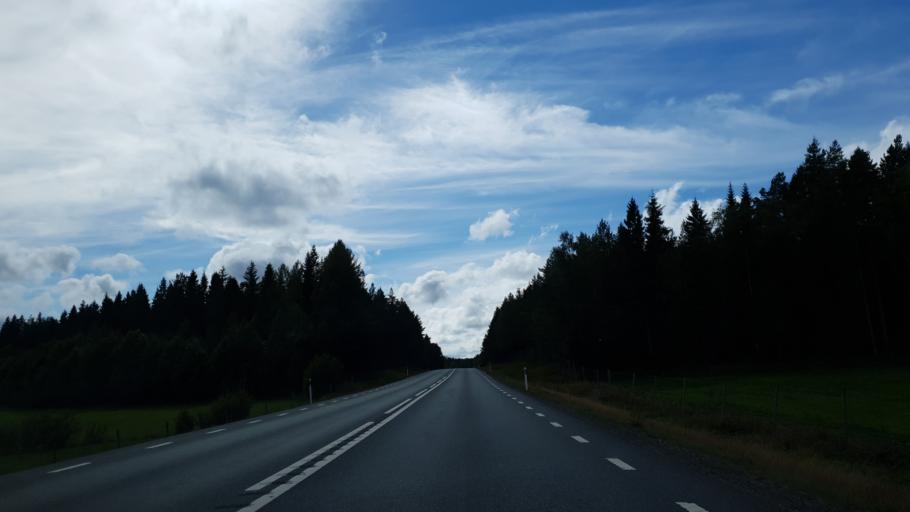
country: SE
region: Vaesterbotten
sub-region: Robertsfors Kommun
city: Robertsfors
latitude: 64.0071
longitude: 20.8051
